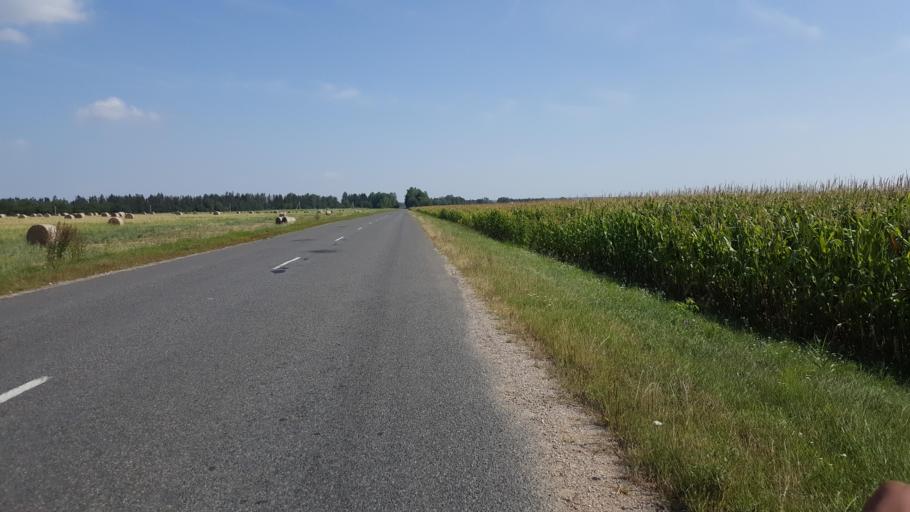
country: BY
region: Brest
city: Kamyanyets
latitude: 52.4187
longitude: 23.7791
